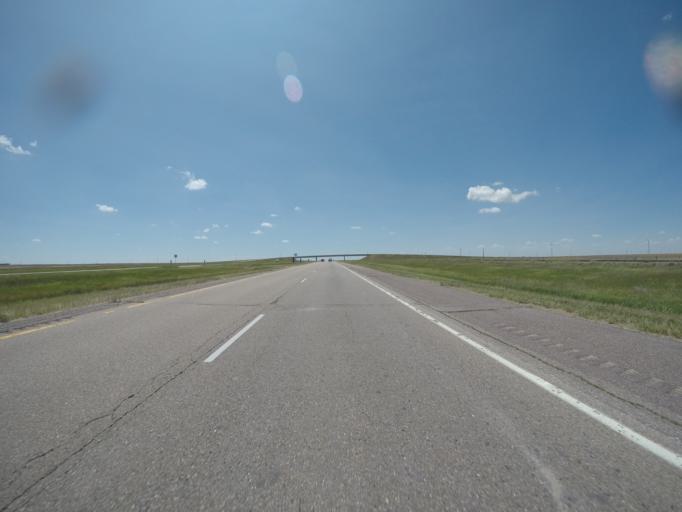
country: US
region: Colorado
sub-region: Lincoln County
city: Hugo
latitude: 39.2815
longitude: -103.3361
